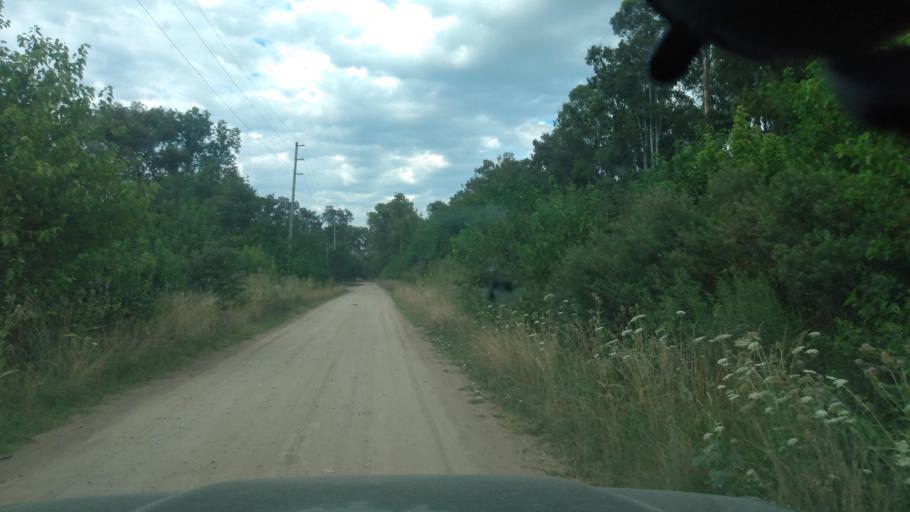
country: AR
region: Buenos Aires
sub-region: Partido de Lujan
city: Lujan
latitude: -34.5973
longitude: -59.0568
